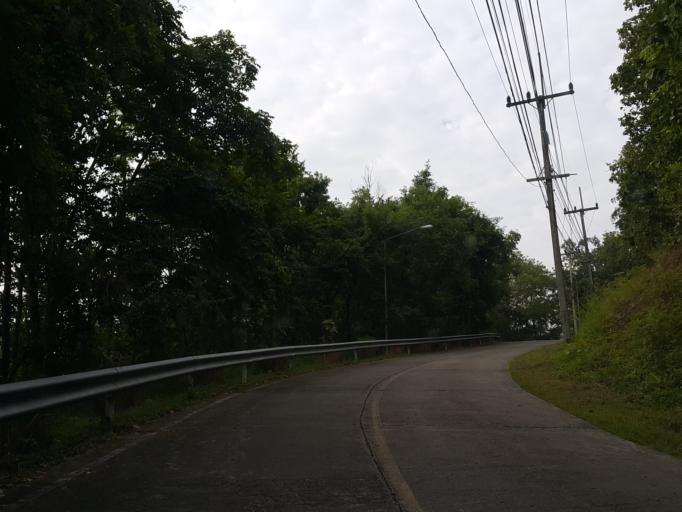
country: TH
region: Mae Hong Son
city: Mae Hong Son
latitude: 19.2984
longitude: 97.9618
